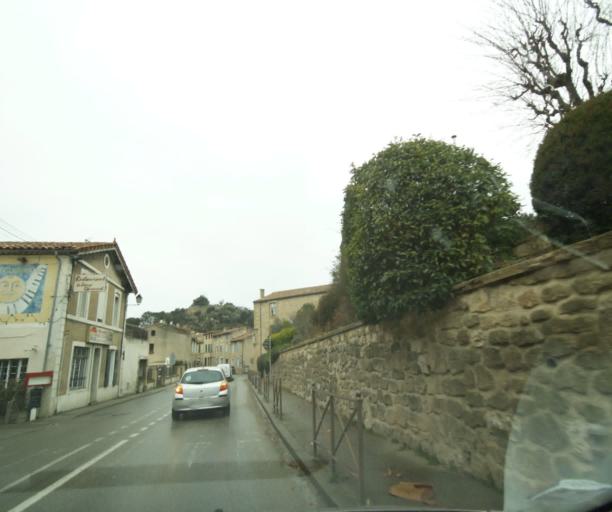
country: FR
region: Provence-Alpes-Cote d'Azur
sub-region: Departement des Bouches-du-Rhone
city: Rognes
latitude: 43.6628
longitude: 5.3495
